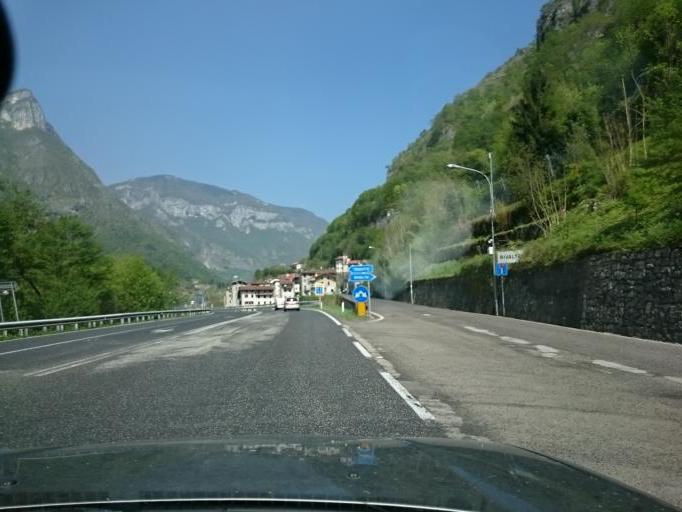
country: IT
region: Veneto
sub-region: Provincia di Vicenza
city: Valstagna
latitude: 45.8775
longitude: 11.6792
